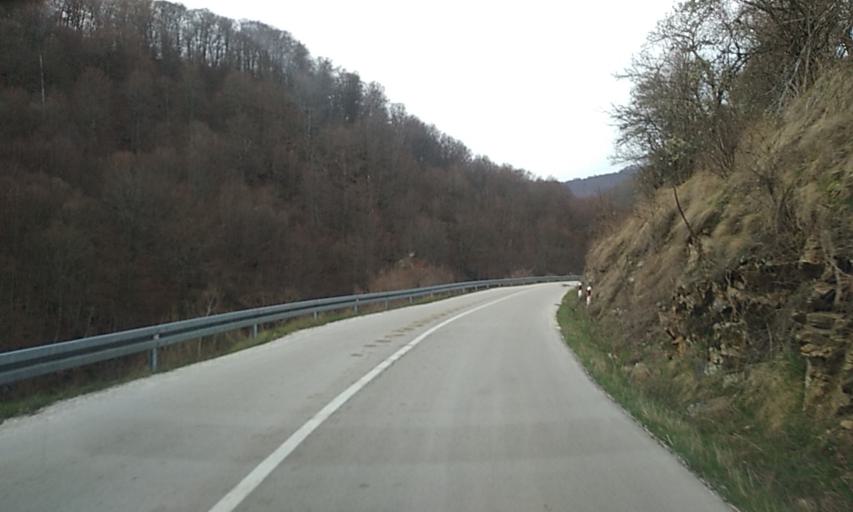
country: RS
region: Central Serbia
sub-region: Pcinjski Okrug
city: Bosilegrad
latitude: 42.5760
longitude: 22.4049
